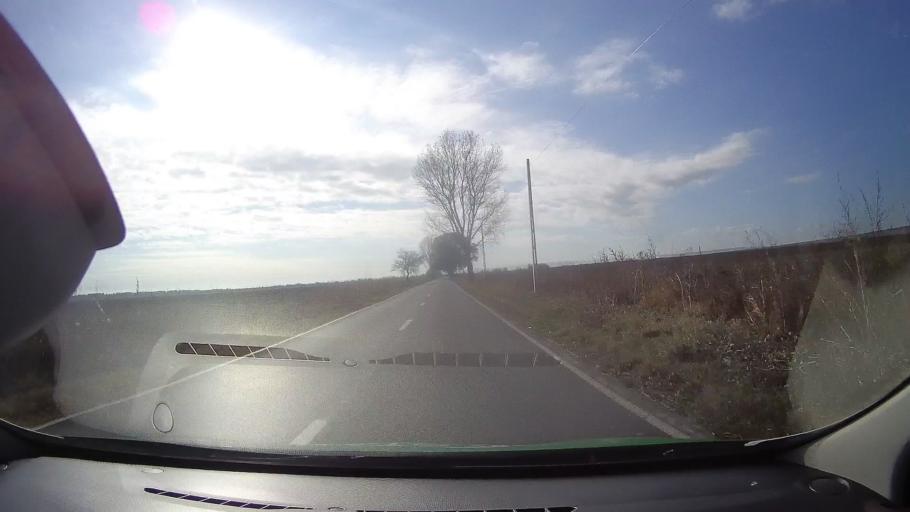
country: RO
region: Tulcea
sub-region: Comuna Valea Nucarilor
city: Agighiol
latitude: 44.9925
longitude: 28.8859
